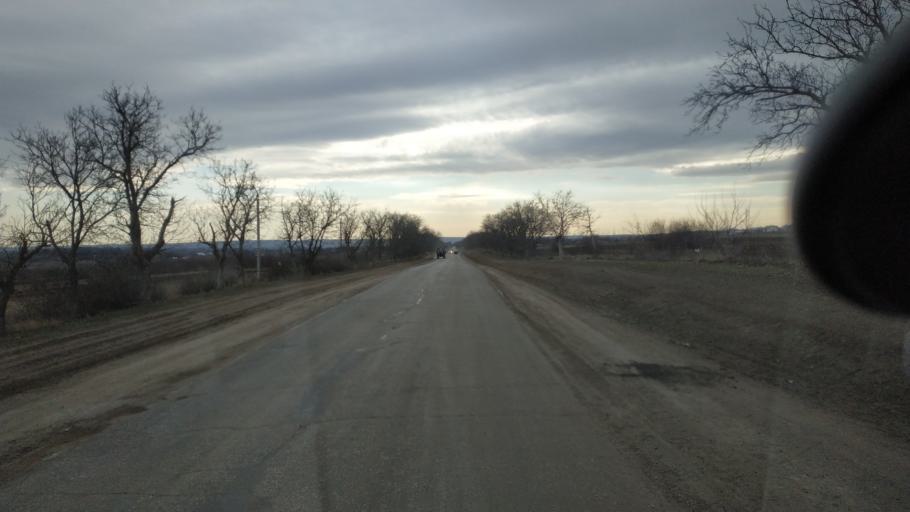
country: MD
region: Criuleni
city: Criuleni
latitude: 47.1773
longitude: 29.1338
